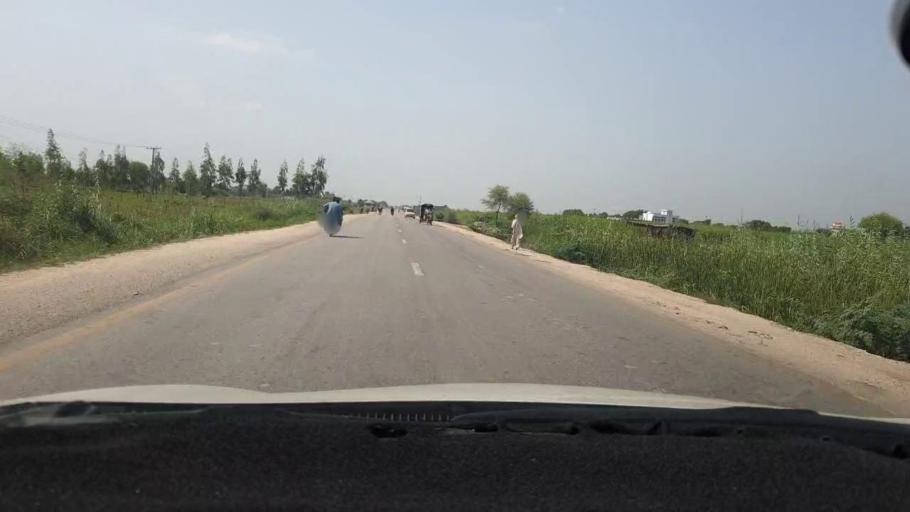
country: PK
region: Sindh
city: Mirpur Khas
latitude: 25.5656
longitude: 69.0614
